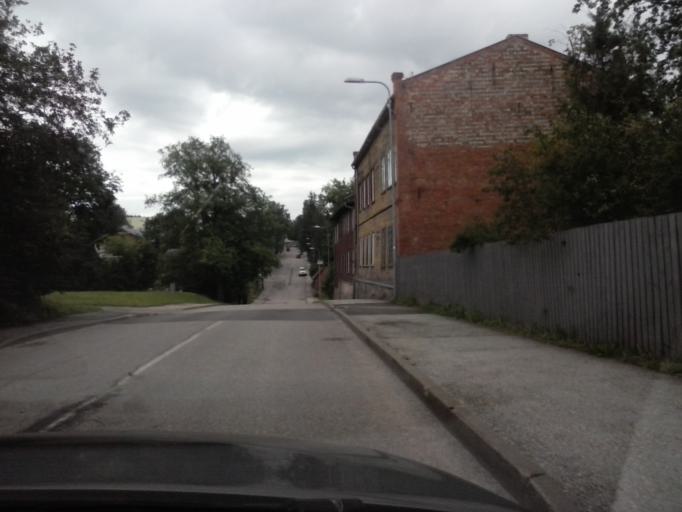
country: EE
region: Valgamaa
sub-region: Valga linn
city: Valga
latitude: 57.7788
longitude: 26.0423
